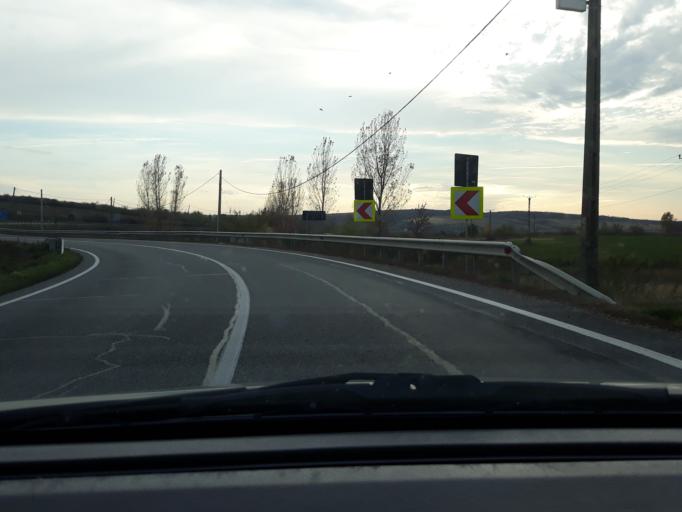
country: RO
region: Bihor
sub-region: Comuna Sacueni
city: Cadea
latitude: 47.3265
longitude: 22.0717
